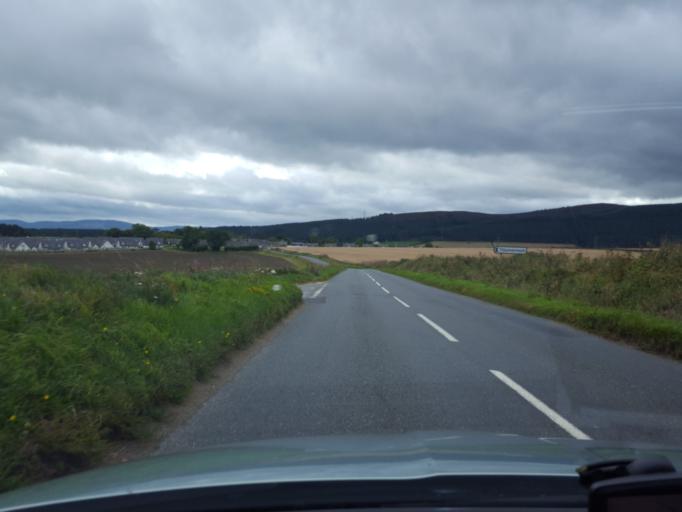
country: GB
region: Scotland
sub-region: Aberdeenshire
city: Kemnay
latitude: 57.1470
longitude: -2.4347
